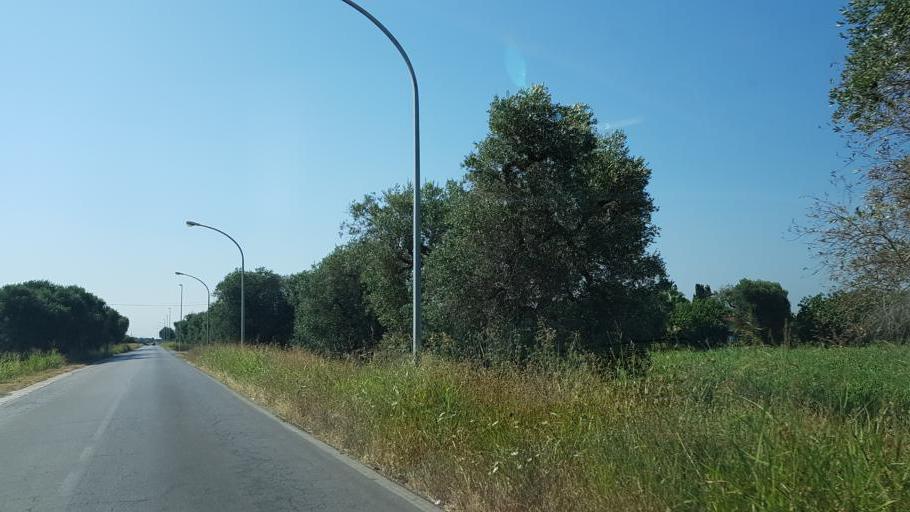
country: IT
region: Apulia
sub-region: Provincia di Brindisi
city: Mesagne
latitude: 40.5484
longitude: 17.8186
